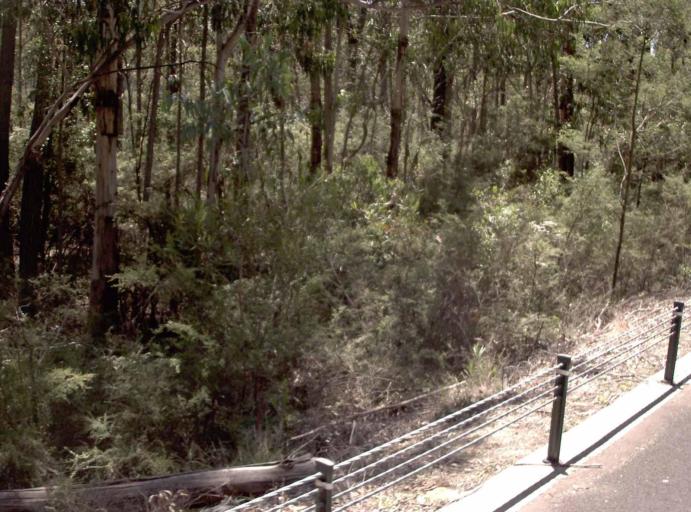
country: AU
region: Victoria
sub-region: East Gippsland
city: Lakes Entrance
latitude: -37.7478
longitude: 148.0711
